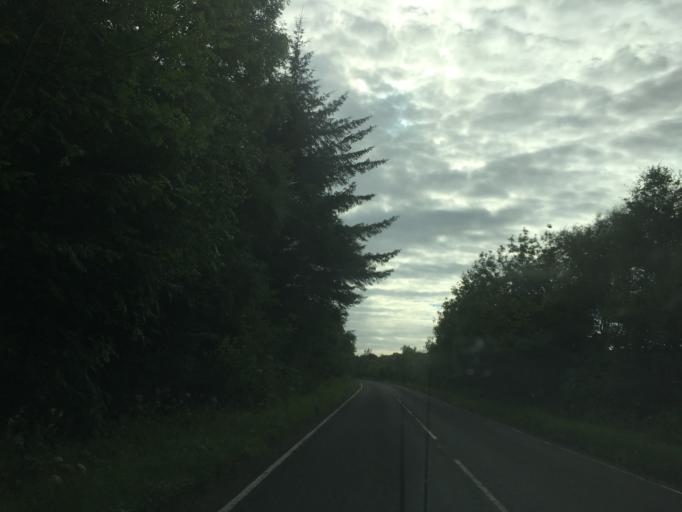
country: GB
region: Scotland
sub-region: Argyll and Bute
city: Oban
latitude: 56.3527
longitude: -5.4935
